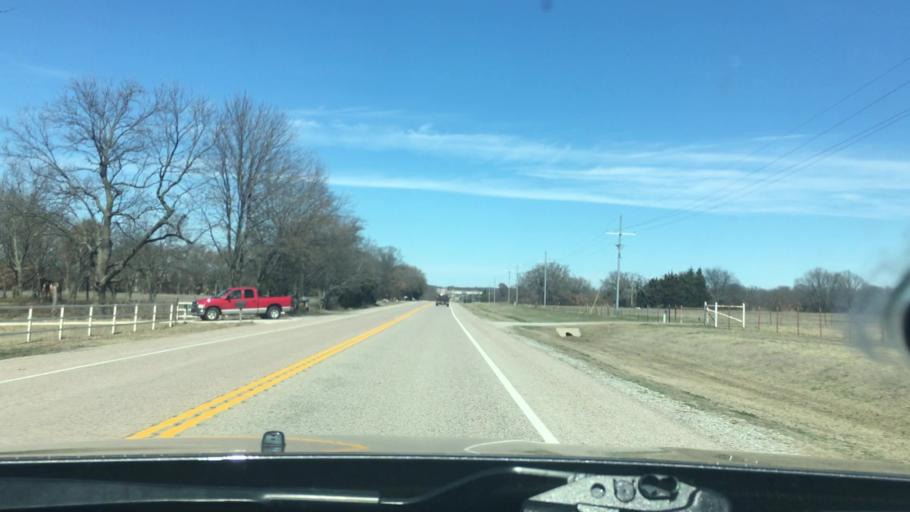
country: US
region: Oklahoma
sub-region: Murray County
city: Sulphur
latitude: 34.4172
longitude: -96.9508
